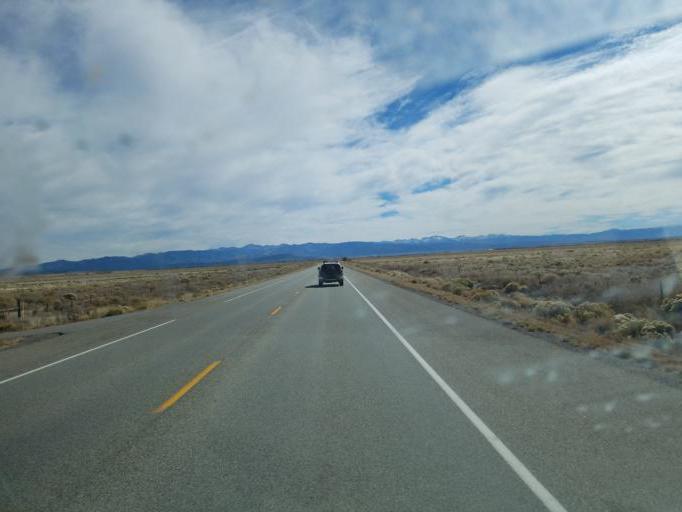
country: US
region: Colorado
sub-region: Alamosa County
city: Alamosa East
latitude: 37.4610
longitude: -105.5607
